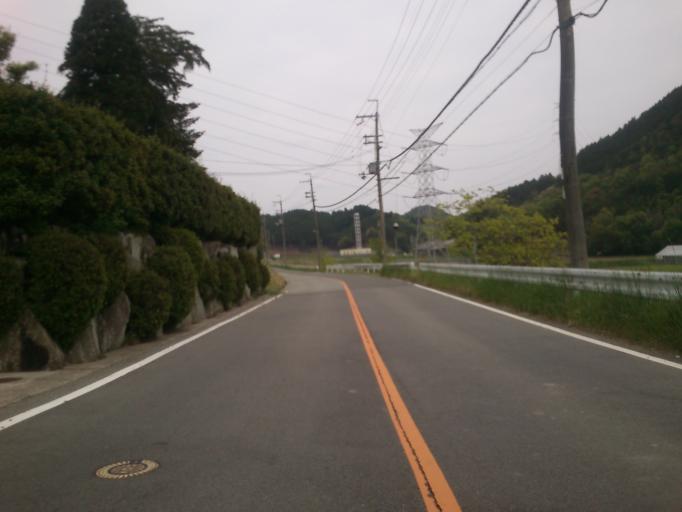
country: JP
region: Kyoto
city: Kameoka
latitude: 34.9728
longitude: 135.5068
